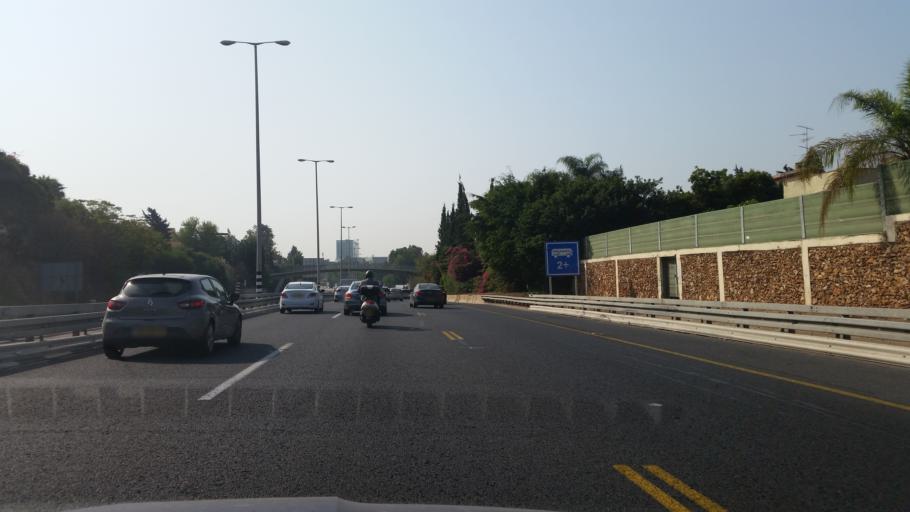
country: IL
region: Tel Aviv
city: Herzliyya
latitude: 32.1735
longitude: 34.8153
